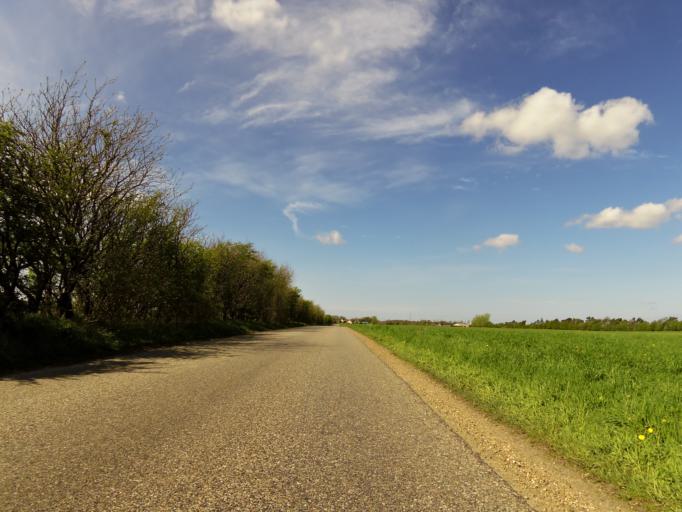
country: DK
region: Central Jutland
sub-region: Skive Kommune
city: Skive
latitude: 56.4621
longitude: 8.9750
